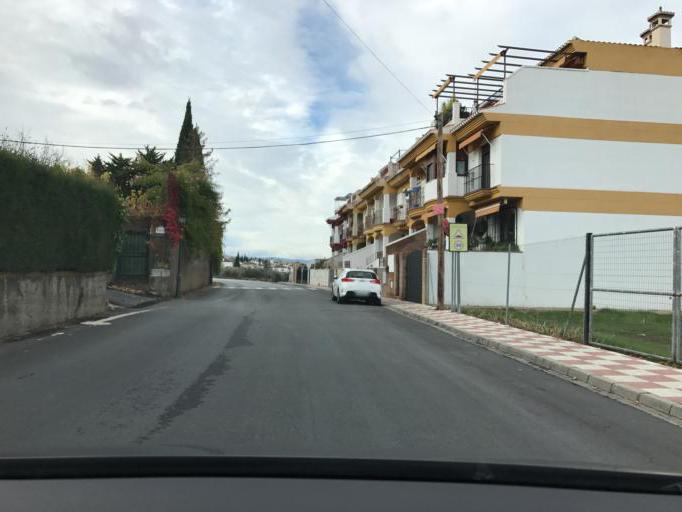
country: ES
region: Andalusia
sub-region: Provincia de Granada
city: Cajar
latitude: 37.1286
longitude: -3.5742
